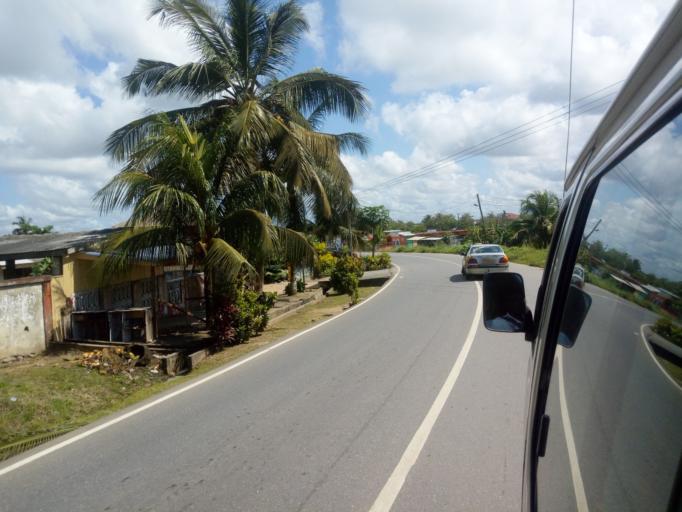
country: GH
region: Central
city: Elmina
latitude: 5.0949
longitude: -1.3356
